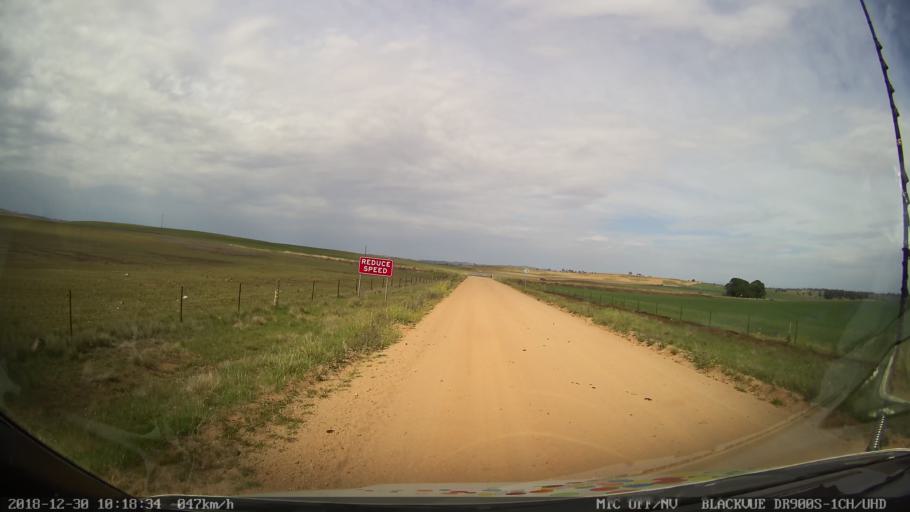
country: AU
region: New South Wales
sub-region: Snowy River
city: Berridale
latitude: -36.5524
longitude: 149.0083
